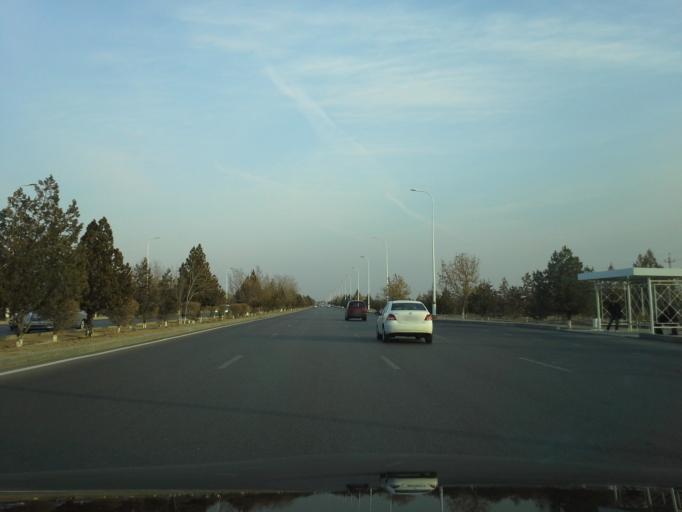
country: TM
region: Ahal
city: Abadan
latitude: 38.0401
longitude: 58.2119
